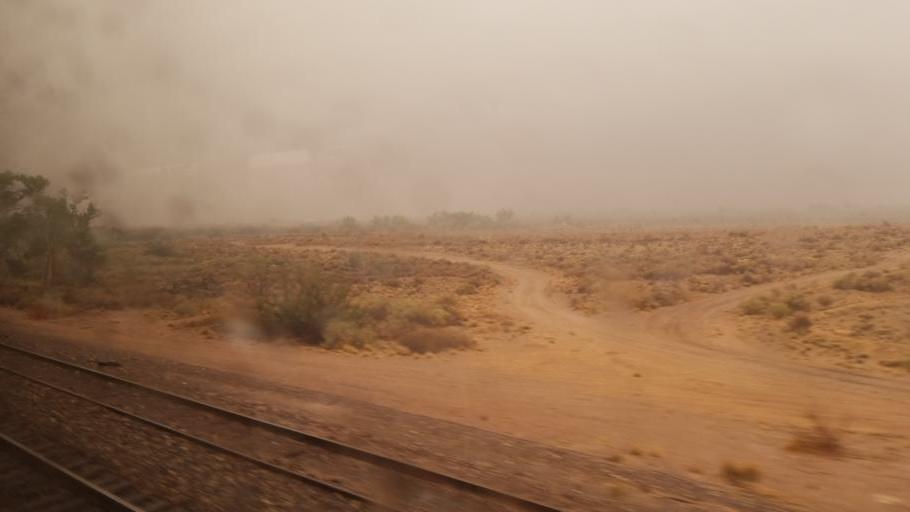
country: US
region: Arizona
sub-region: Navajo County
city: Joseph City
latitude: 34.9059
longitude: -110.2562
